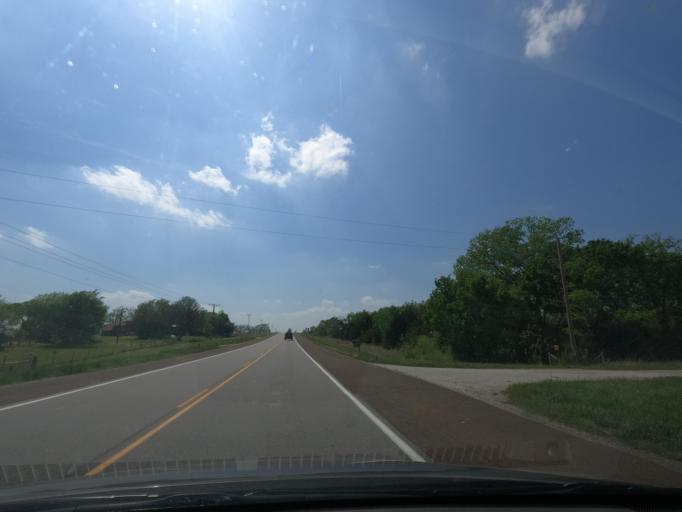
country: US
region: Kansas
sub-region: Butler County
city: El Dorado
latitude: 37.6794
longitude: -96.8117
